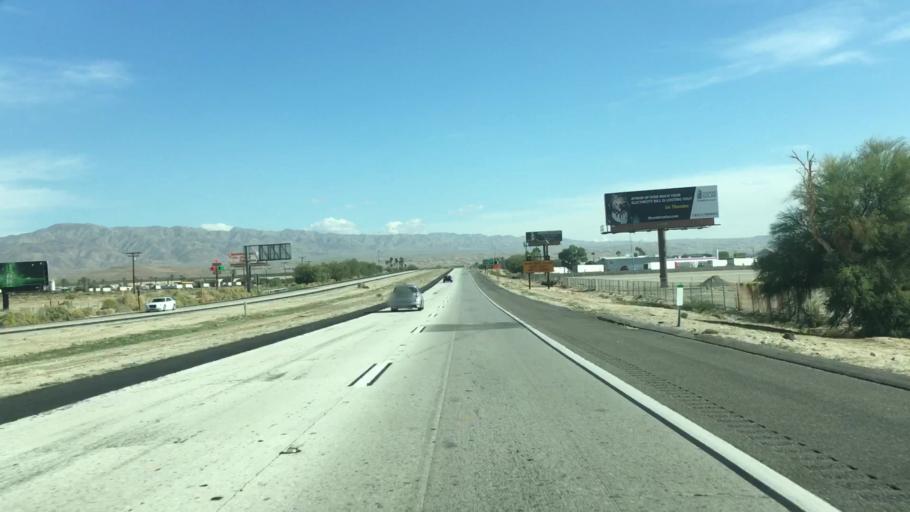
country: US
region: California
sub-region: Riverside County
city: Coachella
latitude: 33.7149
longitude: -116.1814
